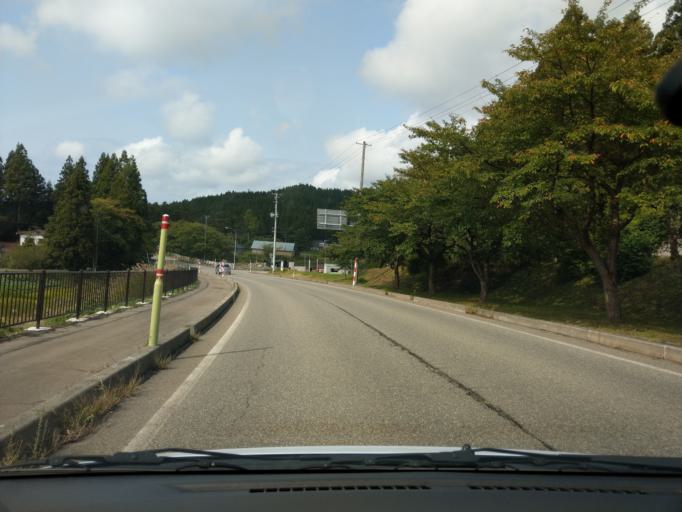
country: JP
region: Akita
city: Omagari
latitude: 39.4407
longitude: 140.3554
